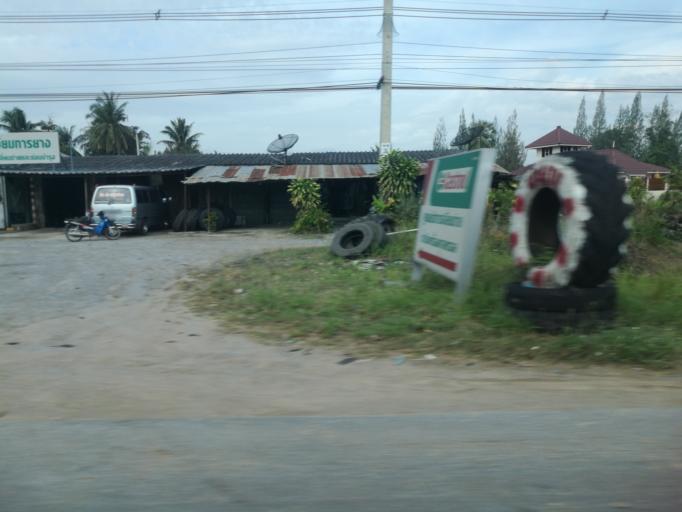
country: TH
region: Prachuap Khiri Khan
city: Hua Hin
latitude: 12.6638
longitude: 99.8766
